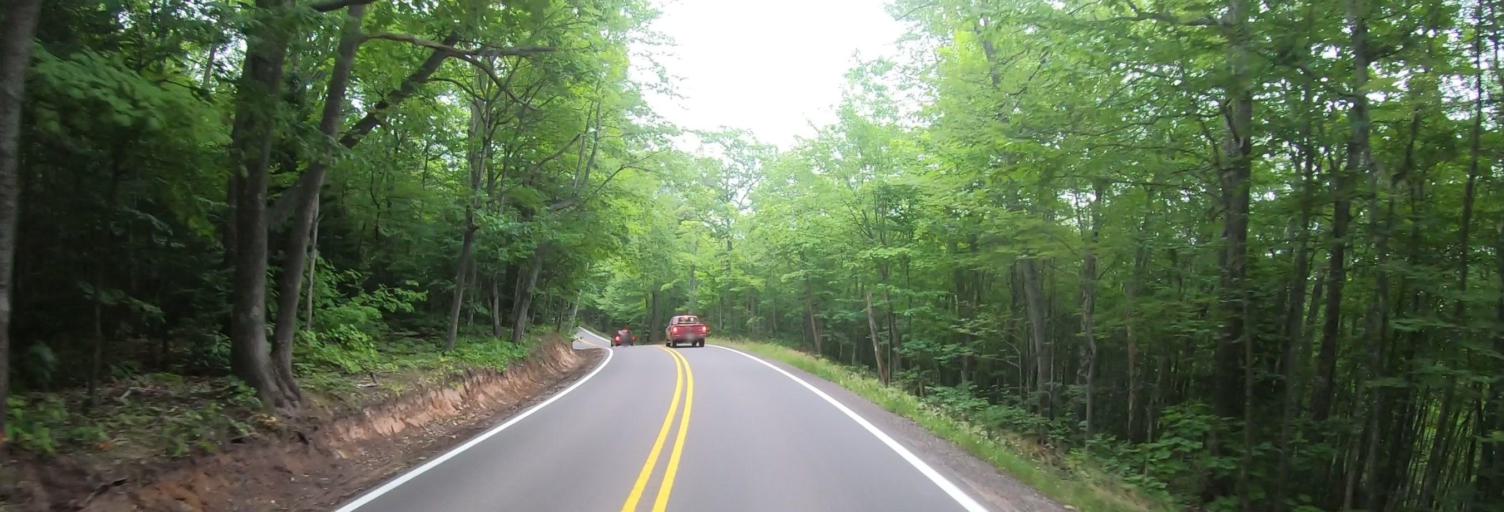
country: US
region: Michigan
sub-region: Keweenaw County
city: Eagle River
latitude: 47.4272
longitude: -87.9922
